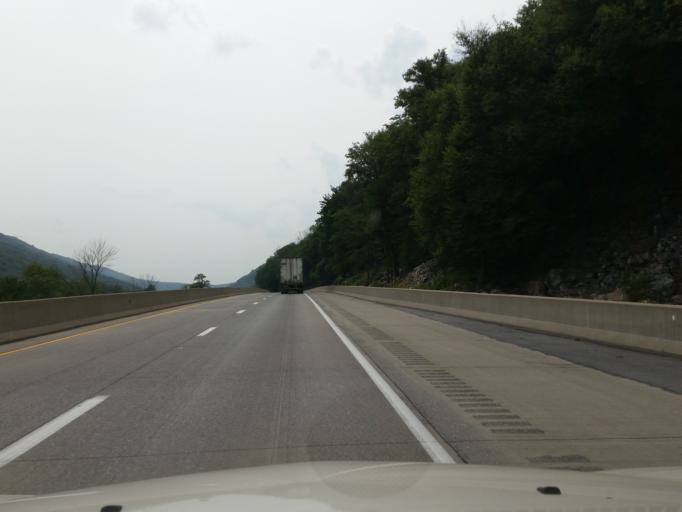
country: US
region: Pennsylvania
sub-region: Mifflin County
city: Highland Park
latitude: 40.6017
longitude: -77.4873
